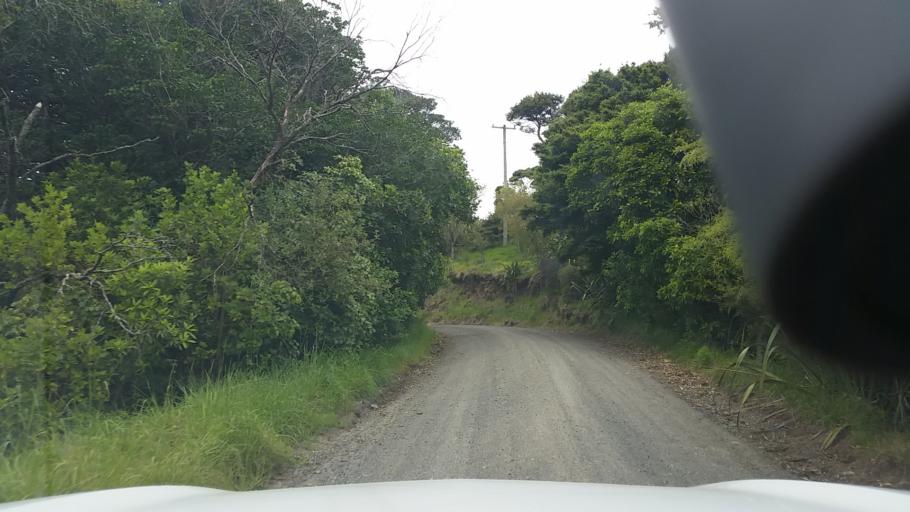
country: NZ
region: Auckland
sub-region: Auckland
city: Muriwai Beach
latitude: -36.8762
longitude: 174.4705
